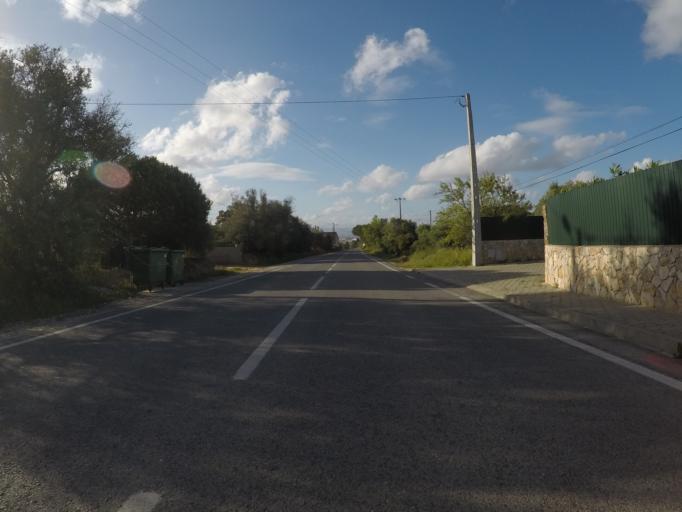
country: PT
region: Faro
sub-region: Lagoa
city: Carvoeiro
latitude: 37.1020
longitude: -8.4440
